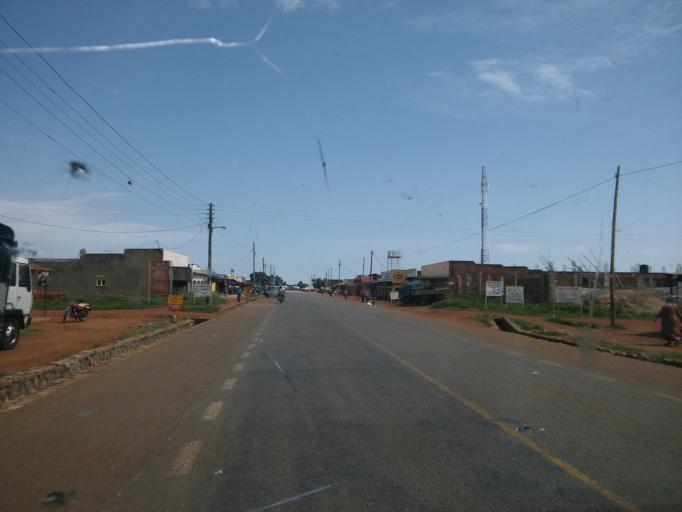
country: UG
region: Eastern Region
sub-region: Bukedea District
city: Bukedea
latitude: 1.3477
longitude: 34.0444
